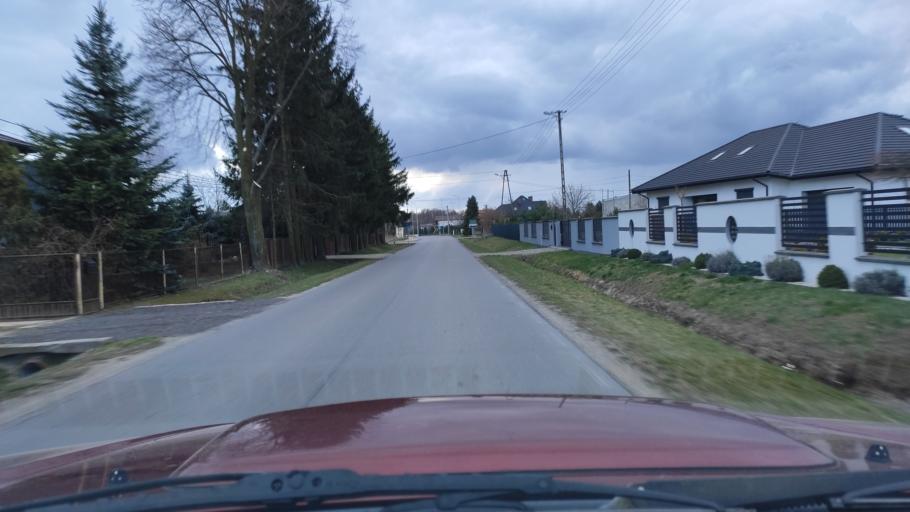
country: PL
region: Masovian Voivodeship
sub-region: Powiat zwolenski
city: Zwolen
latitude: 51.3784
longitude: 21.5978
